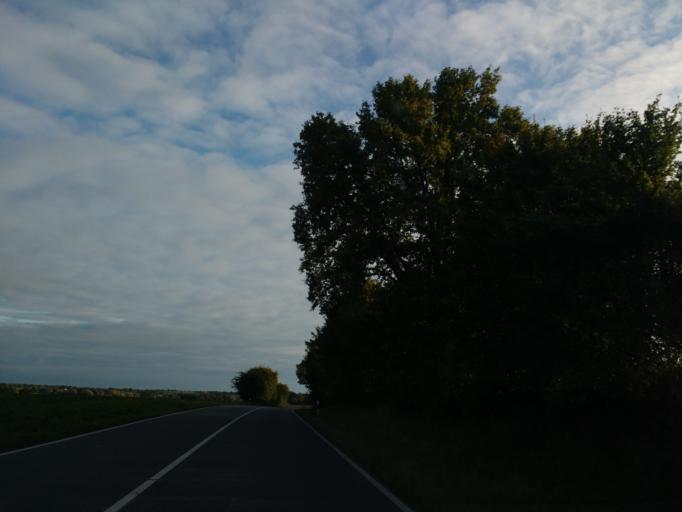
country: DE
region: Schleswig-Holstein
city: Altenkrempe
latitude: 54.1495
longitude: 10.8191
